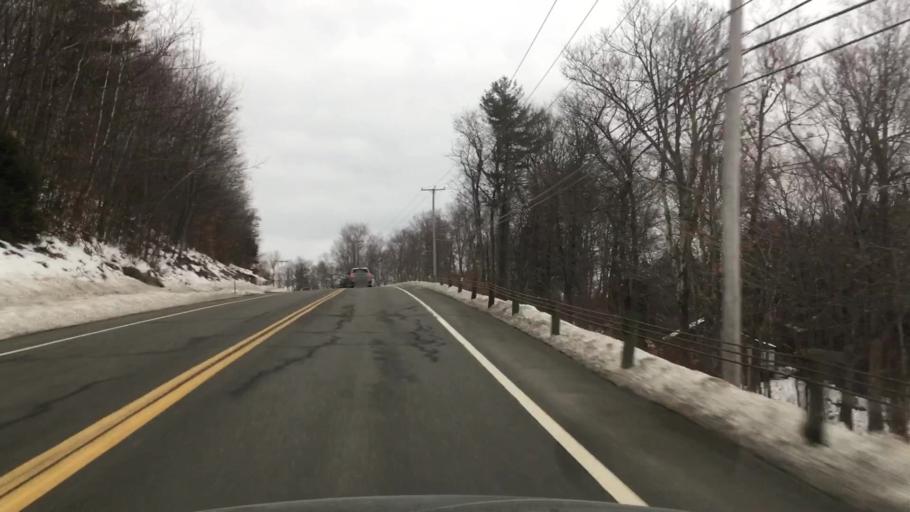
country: US
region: New Hampshire
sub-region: Merrimack County
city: Newbury
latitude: 43.3304
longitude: -72.0445
